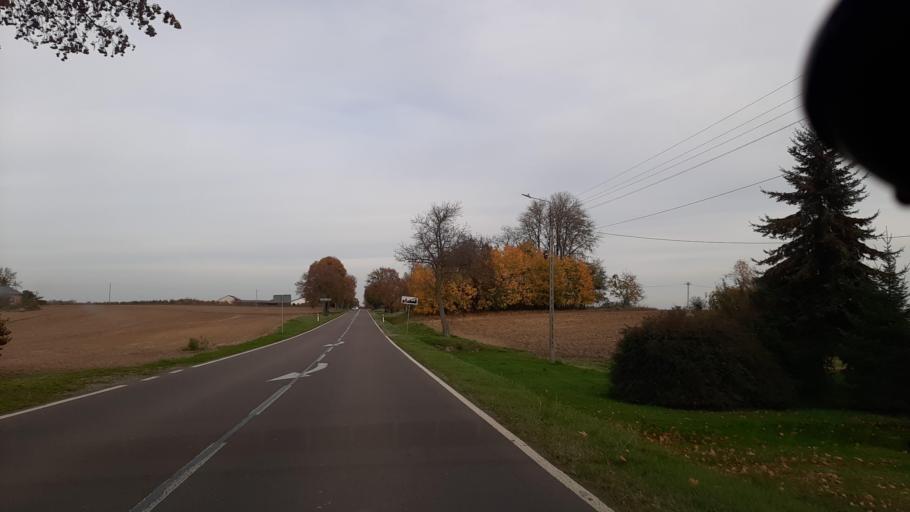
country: PL
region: Lublin Voivodeship
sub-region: Powiat pulawski
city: Markuszow
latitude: 51.3503
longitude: 22.2702
